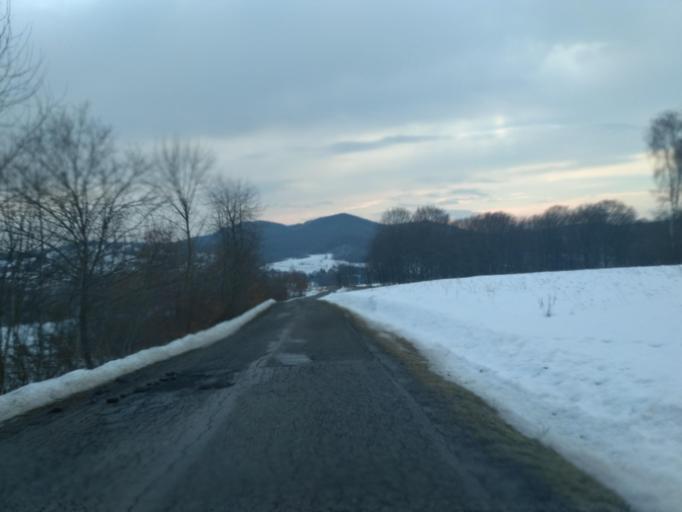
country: PL
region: Subcarpathian Voivodeship
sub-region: Powiat brzozowski
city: Dydnia
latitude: 49.6417
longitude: 22.1617
